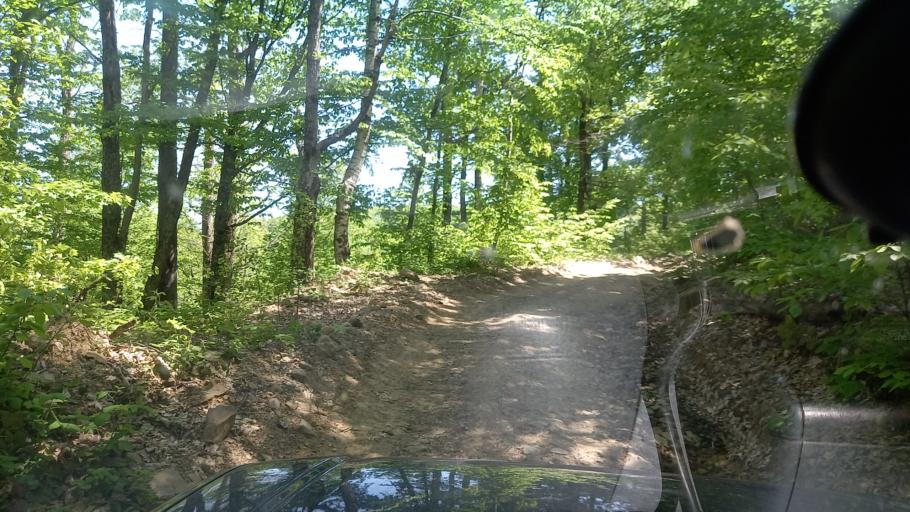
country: RU
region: Krasnodarskiy
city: Tuapse
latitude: 44.2630
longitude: 39.2823
